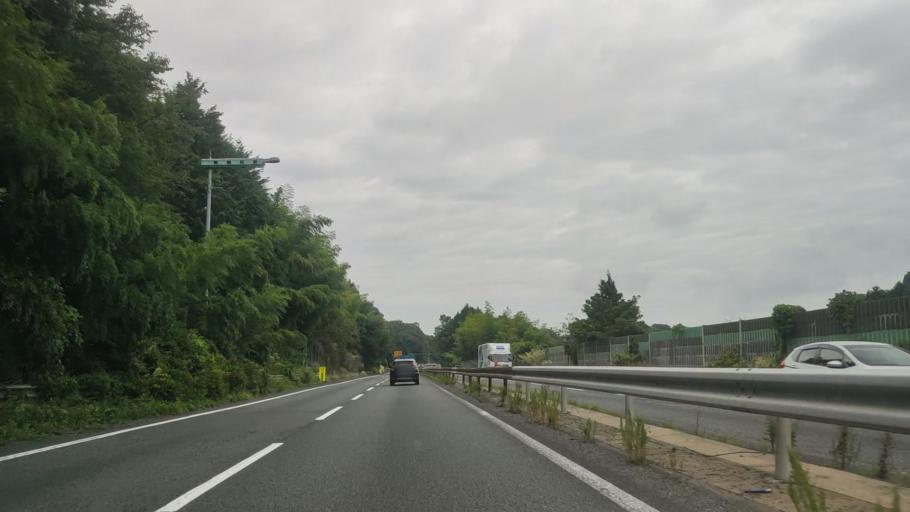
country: JP
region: Mie
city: Nabari
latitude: 34.6410
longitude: 136.0072
